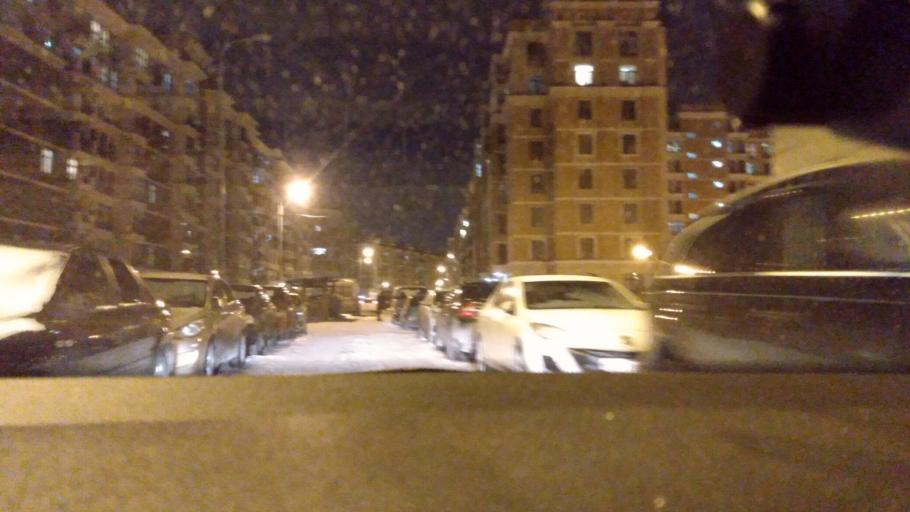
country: RU
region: Moskovskaya
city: Opalikha
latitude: 55.8157
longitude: 37.2458
